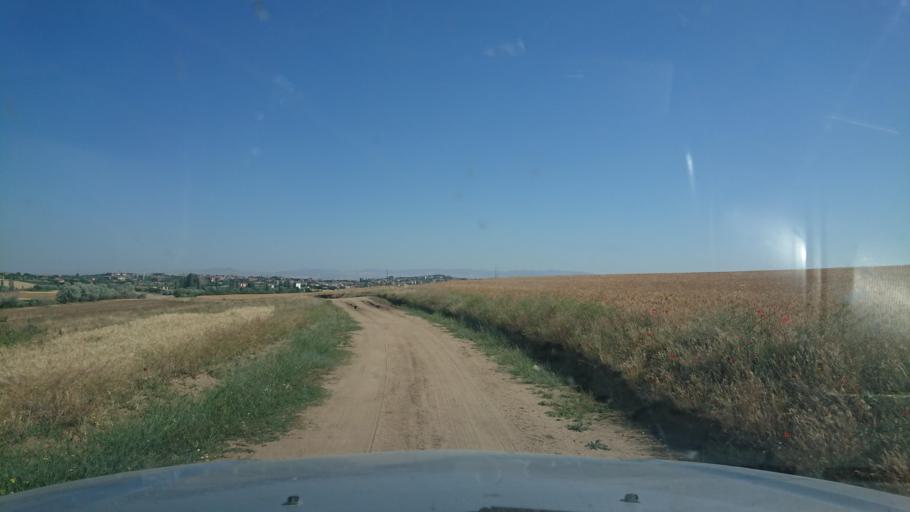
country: TR
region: Aksaray
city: Agacoren
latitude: 38.8535
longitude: 33.9146
